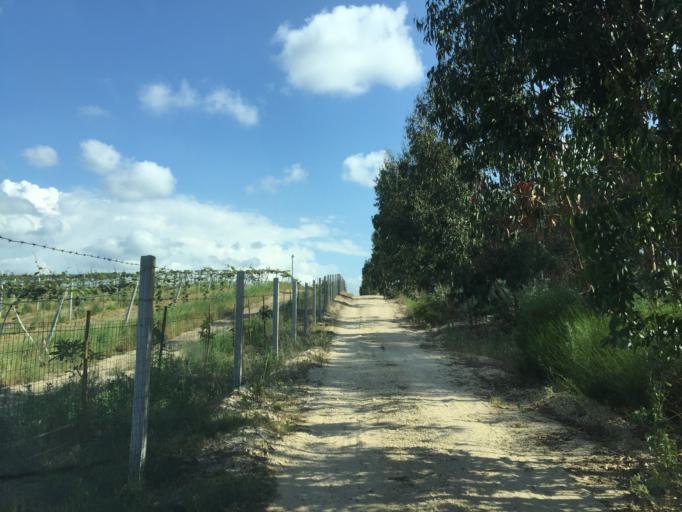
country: PT
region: Leiria
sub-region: Leiria
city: Monte Redondo
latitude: 39.9457
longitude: -8.8256
